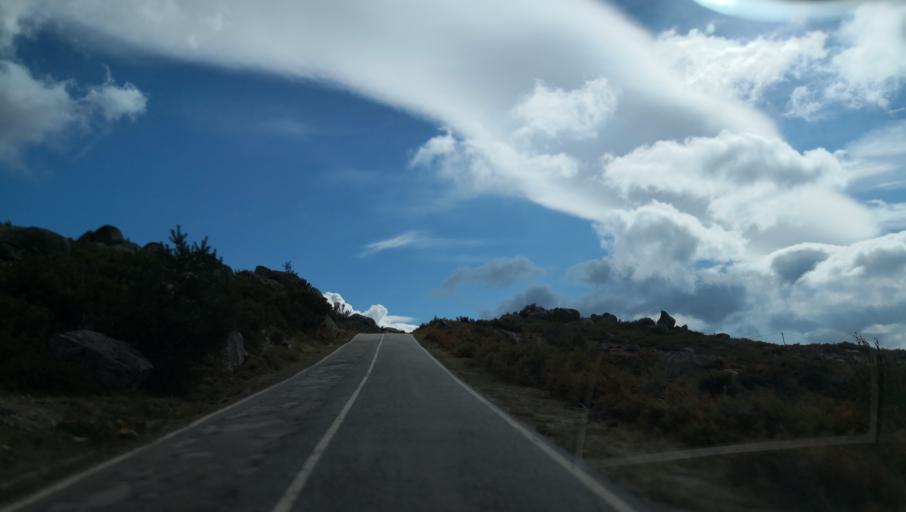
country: PT
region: Vila Real
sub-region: Vila Real
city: Vila Real
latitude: 41.3605
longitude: -7.7966
